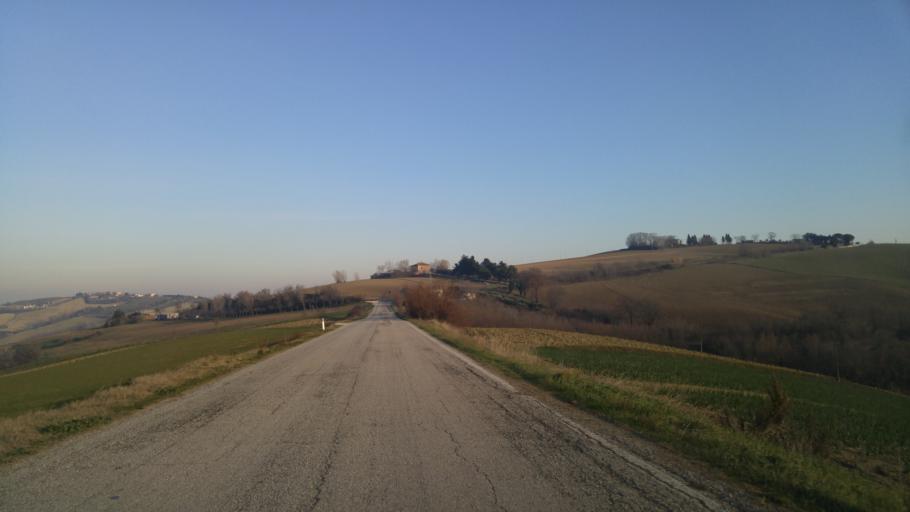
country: IT
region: The Marches
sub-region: Provincia di Pesaro e Urbino
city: San Giorgio di Pesaro
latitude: 43.7100
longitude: 13.0072
